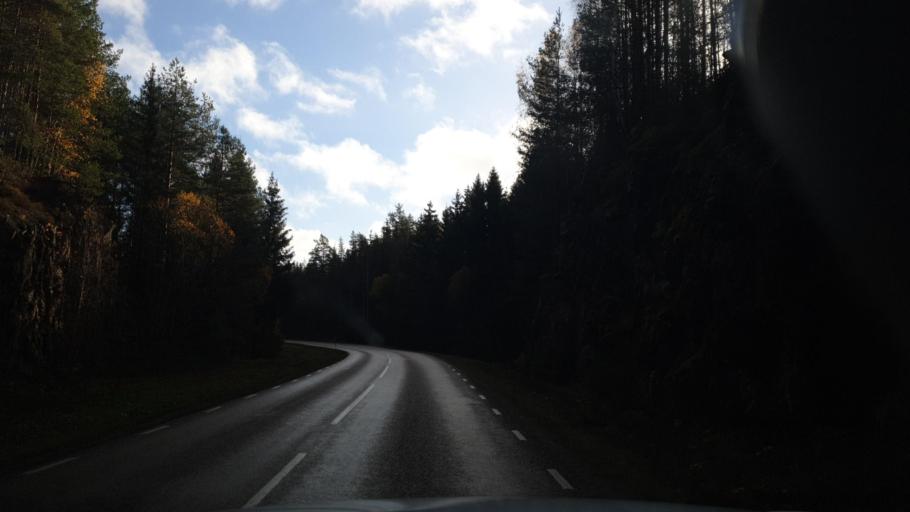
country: SE
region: Vaermland
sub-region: Grums Kommun
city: Grums
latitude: 59.4005
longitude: 13.0183
